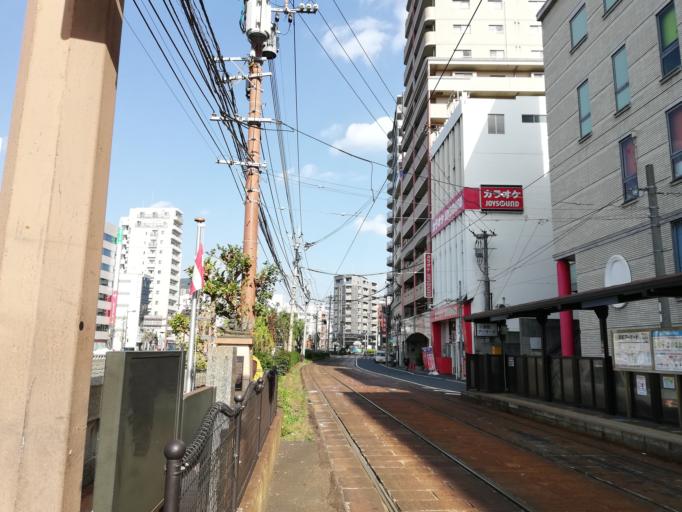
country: JP
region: Nagasaki
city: Nagasaki-shi
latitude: 32.7448
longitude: 129.8768
